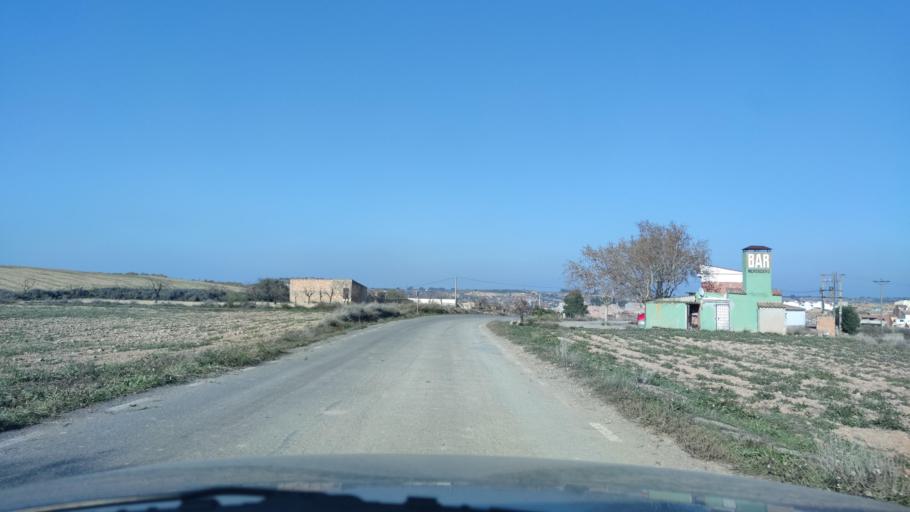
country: ES
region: Catalonia
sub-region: Provincia de Lleida
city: Torrebesses
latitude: 41.4550
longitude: 0.5577
